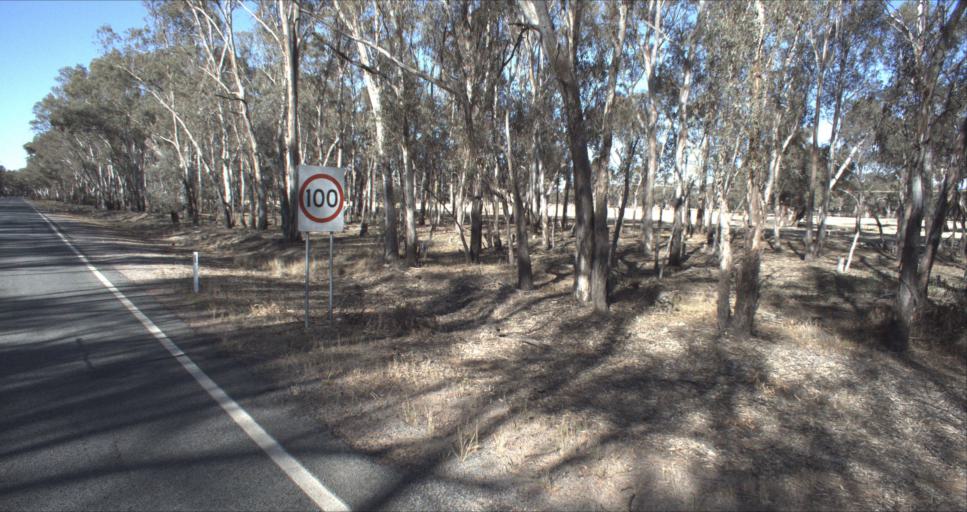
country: AU
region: New South Wales
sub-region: Leeton
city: Leeton
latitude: -34.6294
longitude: 146.3768
